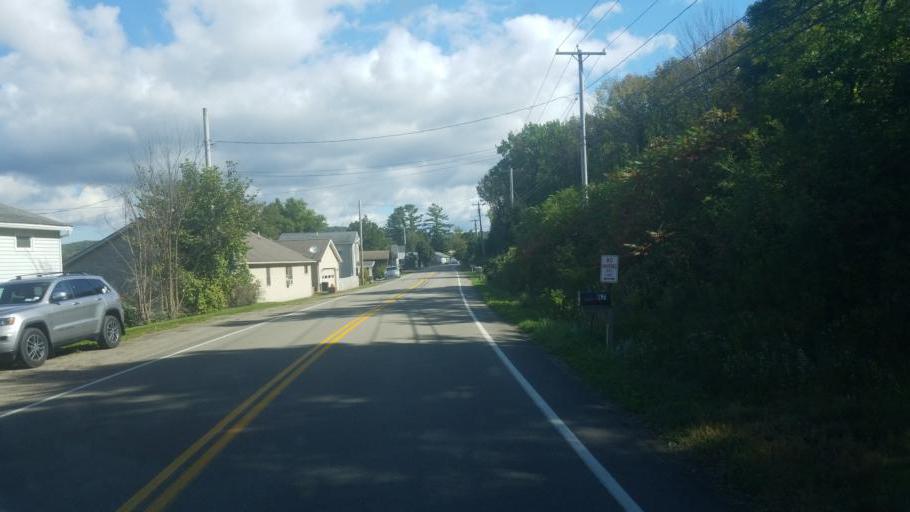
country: US
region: New York
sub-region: Allegany County
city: Cuba
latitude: 42.2430
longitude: -78.3016
